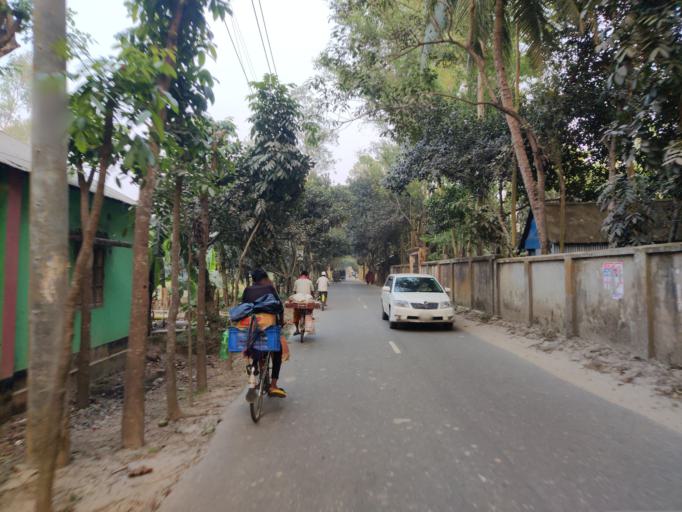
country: BD
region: Dhaka
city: Bajitpur
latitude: 24.1584
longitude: 90.8035
